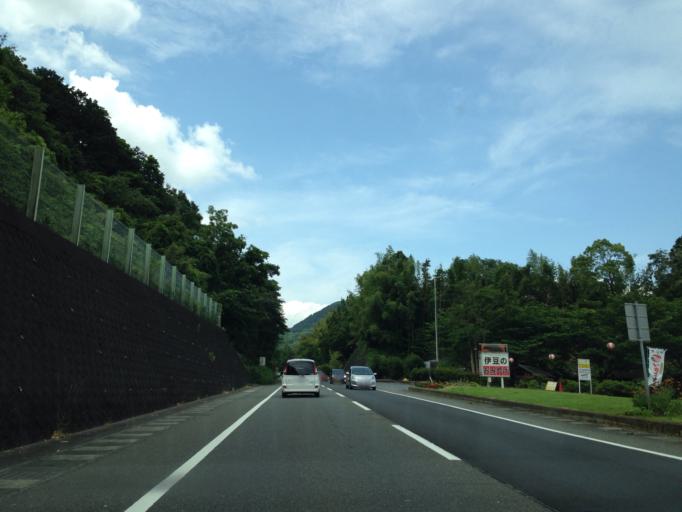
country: JP
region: Shizuoka
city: Mishima
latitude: 35.0495
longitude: 138.9226
